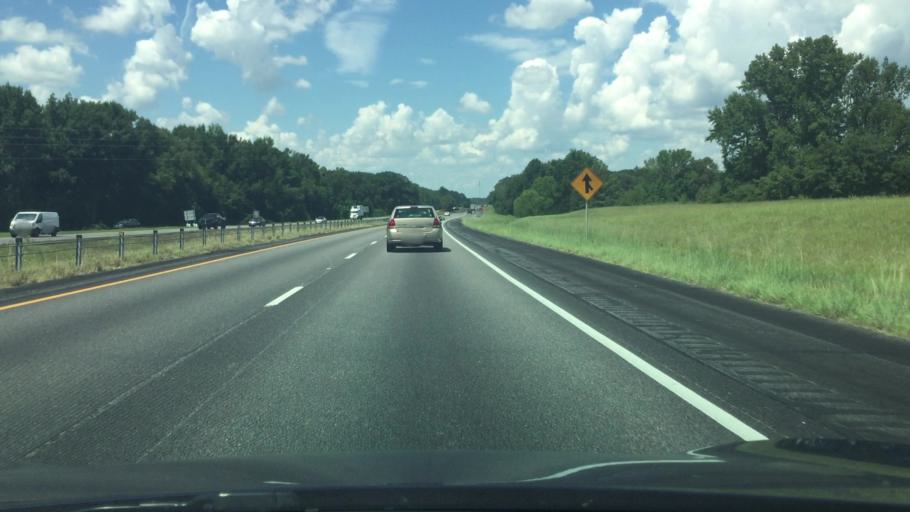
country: US
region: Alabama
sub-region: Elmore County
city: Tallassee
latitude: 32.4280
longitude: -85.9010
